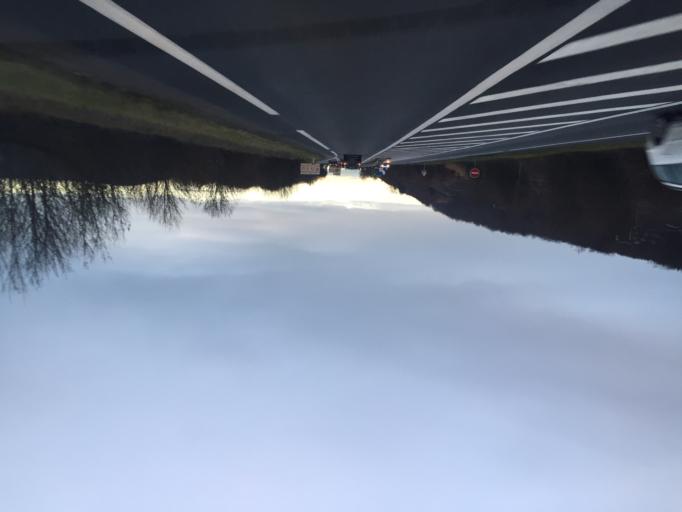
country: FR
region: Bourgogne
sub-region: Departement de Saone-et-Loire
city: La Roche-Vineuse
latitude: 46.3742
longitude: 4.6732
